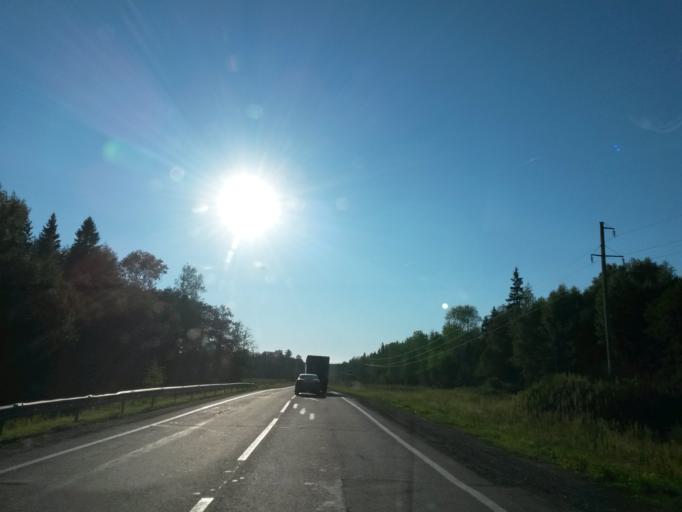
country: RU
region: Jaroslavl
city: Gavrilov-Yam
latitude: 57.2646
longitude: 40.0141
